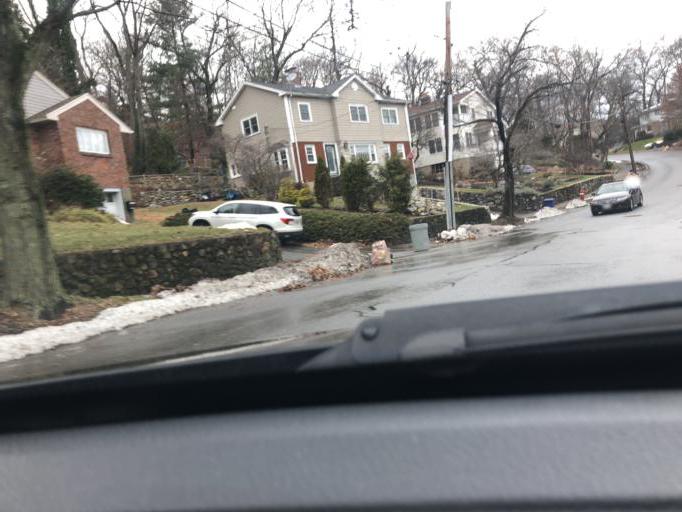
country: US
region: Massachusetts
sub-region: Middlesex County
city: Arlington
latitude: 42.4243
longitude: -71.1573
